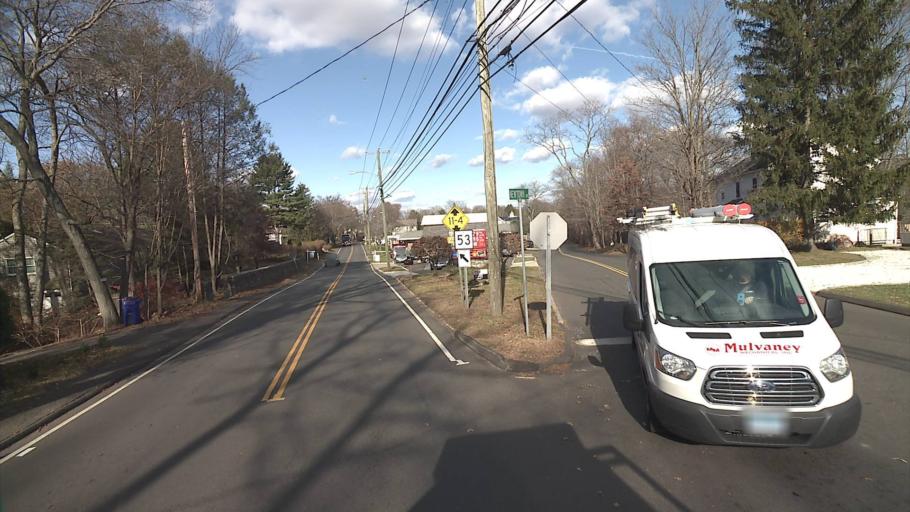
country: US
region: Connecticut
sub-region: Fairfield County
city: Norwalk
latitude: 41.1456
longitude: -73.3948
